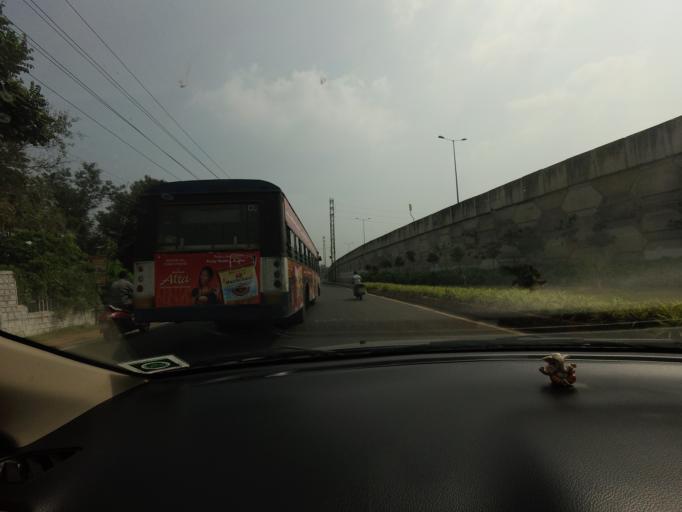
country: IN
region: Andhra Pradesh
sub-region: Krishna
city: Vijayawada
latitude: 16.5013
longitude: 80.6351
